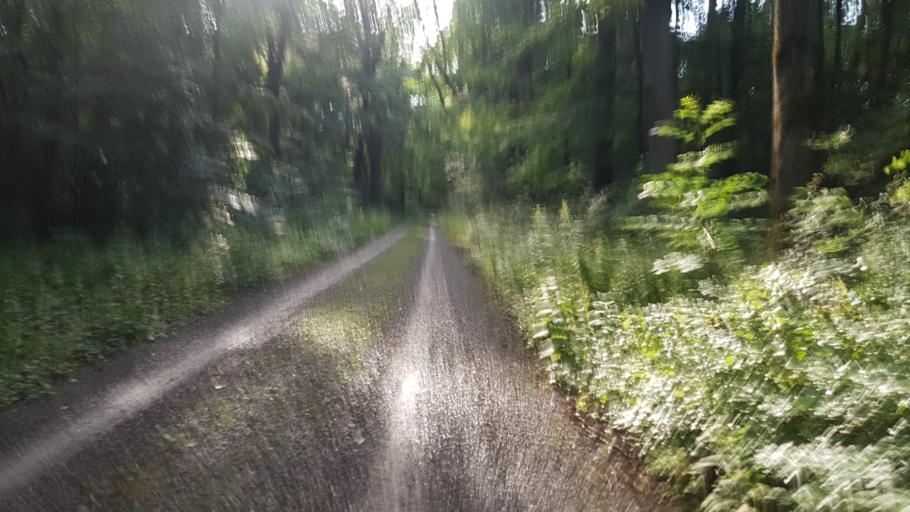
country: DE
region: Baden-Wuerttemberg
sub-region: Regierungsbezirk Stuttgart
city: Zaberfeld
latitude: 49.0405
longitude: 8.9044
